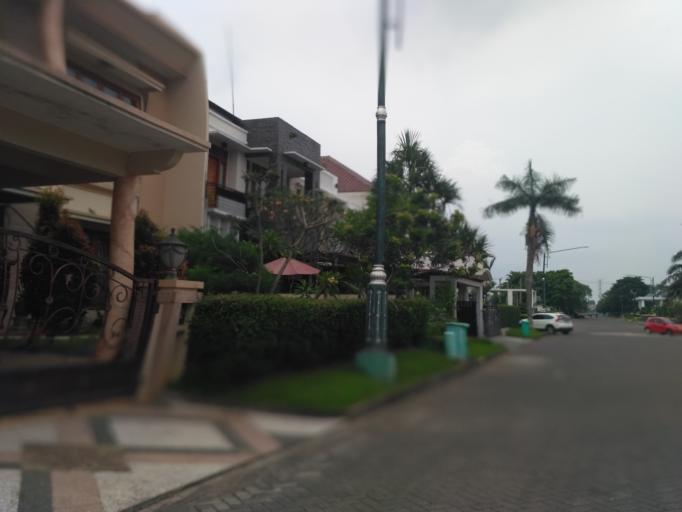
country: ID
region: Central Java
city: Semarang
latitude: -7.0611
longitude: 110.4306
